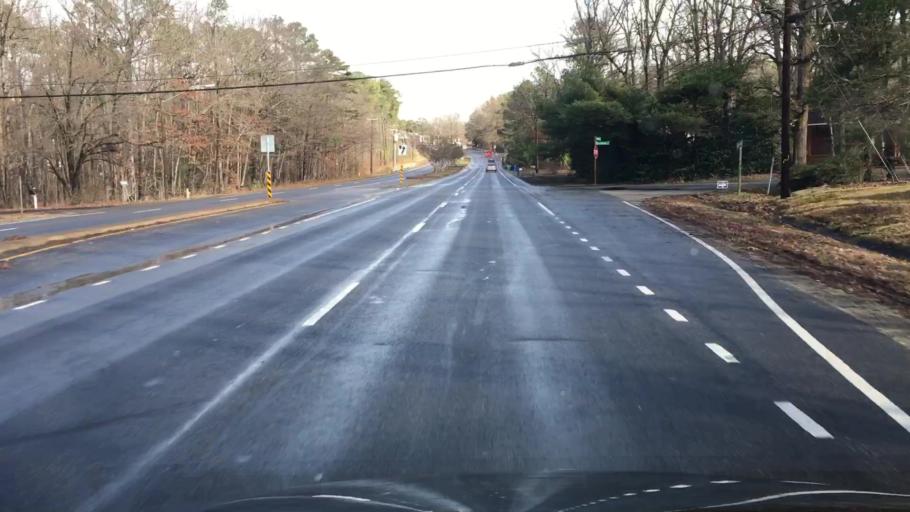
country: US
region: Virginia
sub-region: Chesterfield County
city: Bon Air
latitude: 37.5339
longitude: -77.5711
